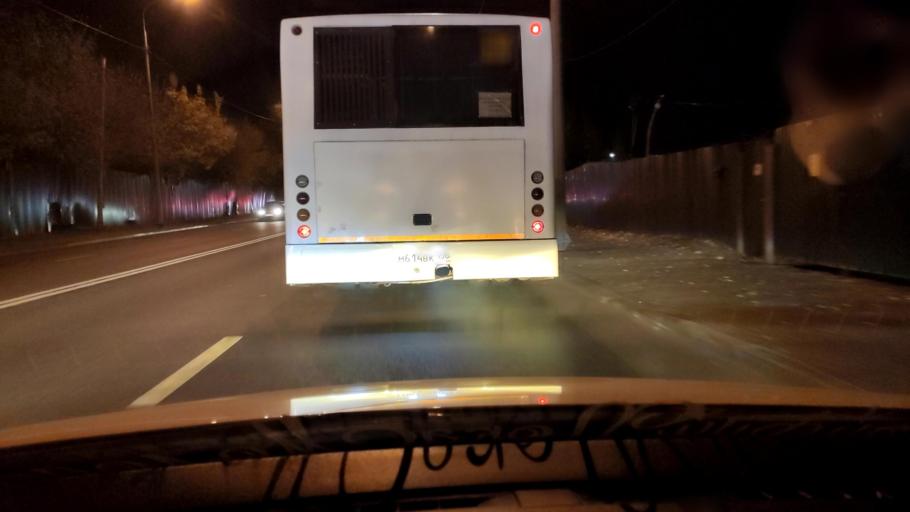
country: RU
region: Voronezj
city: Voronezh
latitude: 51.6906
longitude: 39.2323
